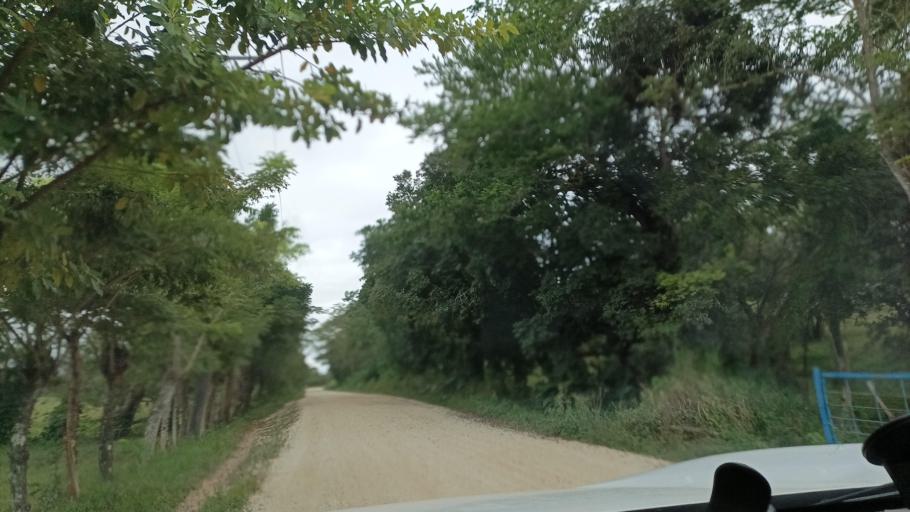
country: MX
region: Veracruz
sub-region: Moloacan
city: Cuichapa
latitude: 17.8437
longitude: -94.3598
